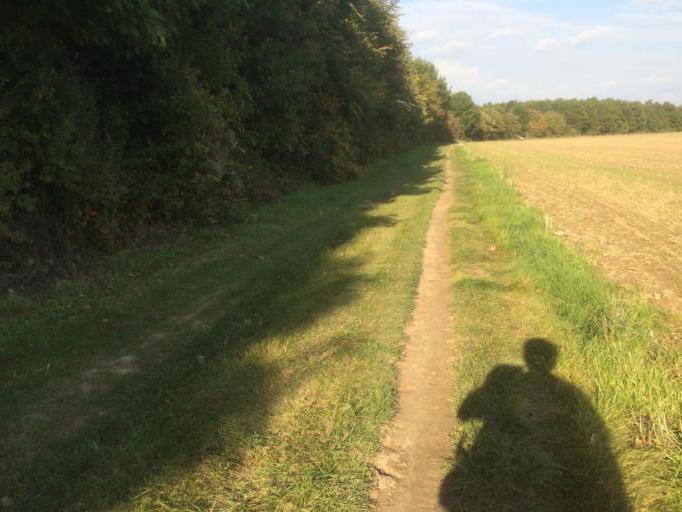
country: FR
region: Ile-de-France
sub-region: Departement des Yvelines
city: Les Loges-en-Josas
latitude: 48.7514
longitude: 2.1313
